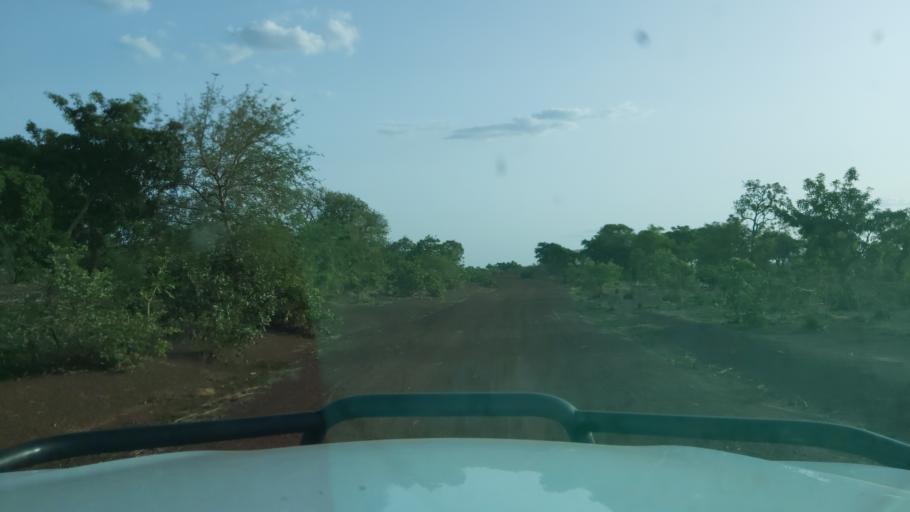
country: ML
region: Koulikoro
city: Kolokani
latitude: 13.2153
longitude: -7.8971
